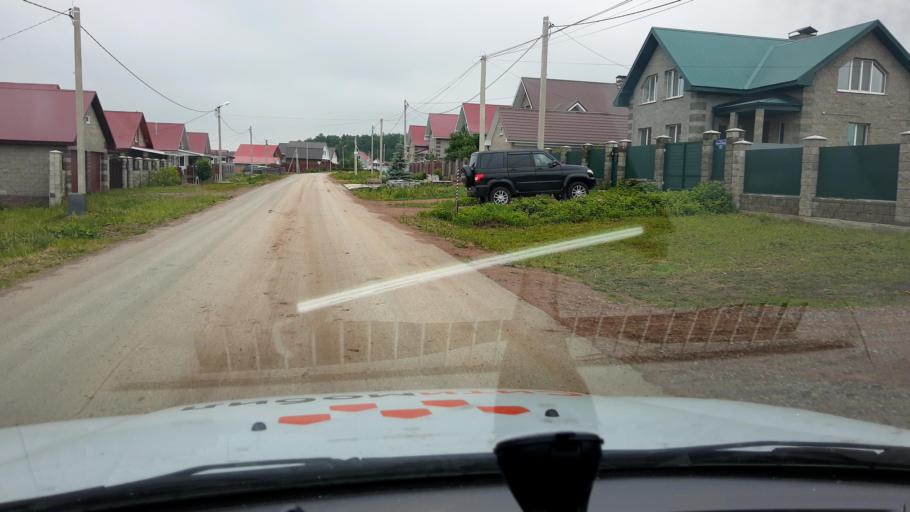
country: RU
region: Bashkortostan
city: Kabakovo
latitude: 54.6647
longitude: 56.2188
